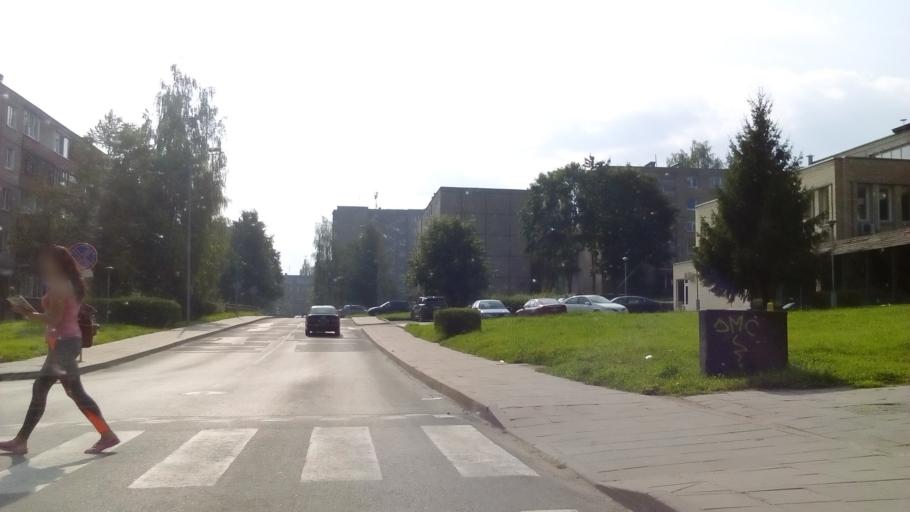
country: LT
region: Alytaus apskritis
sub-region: Alytus
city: Alytus
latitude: 54.3924
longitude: 24.0230
